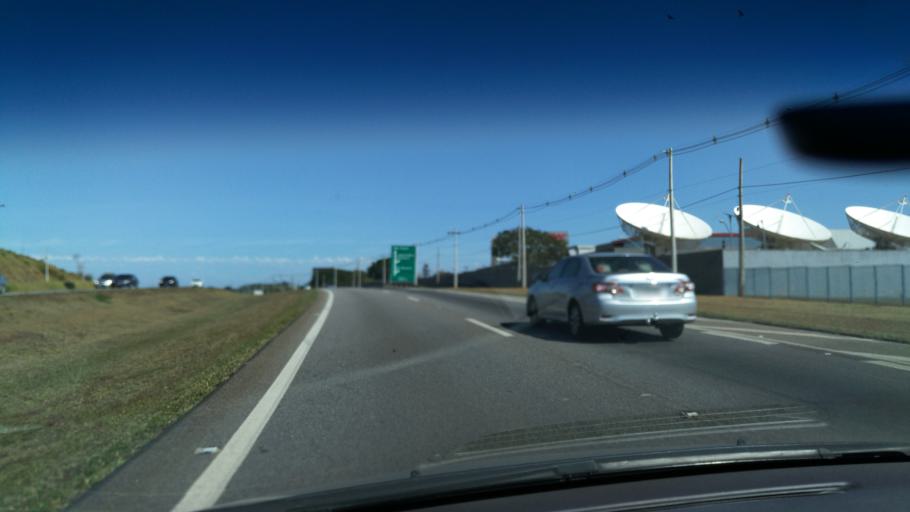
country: BR
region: Sao Paulo
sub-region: Jaguariuna
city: Jaguariuna
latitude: -22.6890
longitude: -47.0120
